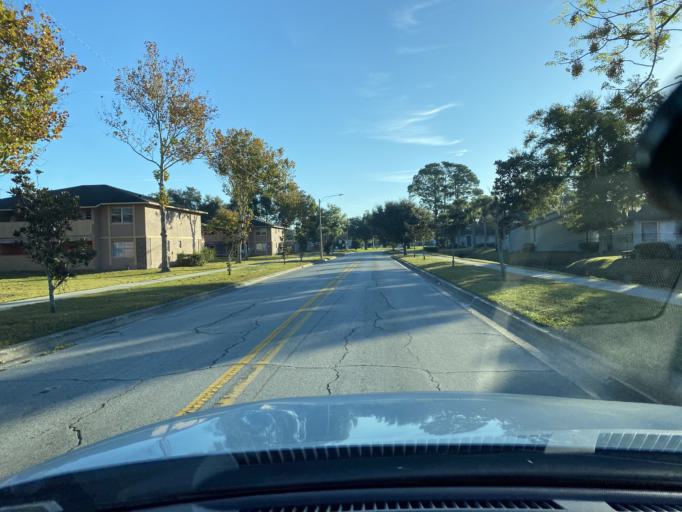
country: US
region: Florida
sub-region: Orange County
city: Azalea Park
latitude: 28.5354
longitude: -81.3077
